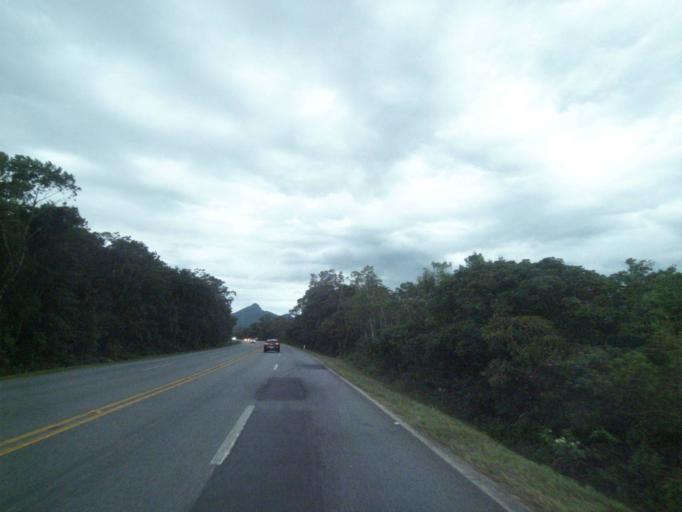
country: BR
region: Parana
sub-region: Pontal Do Parana
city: Pontal do Parana
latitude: -25.7597
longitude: -48.5913
